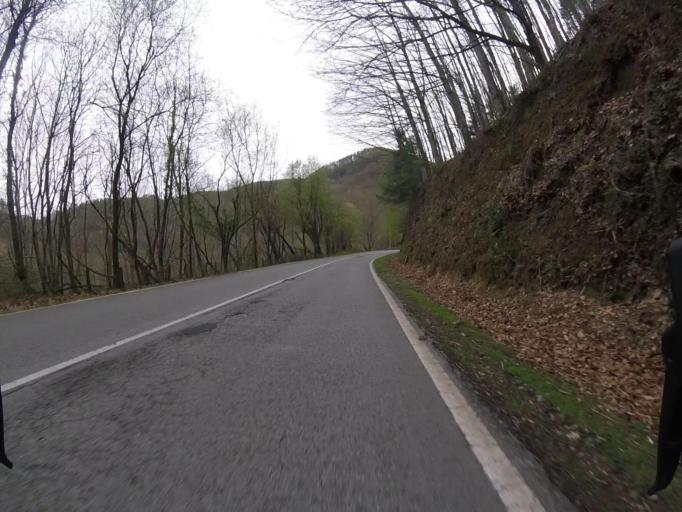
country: ES
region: Basque Country
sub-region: Provincia de Guipuzcoa
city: Irun
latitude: 43.2734
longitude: -1.7765
